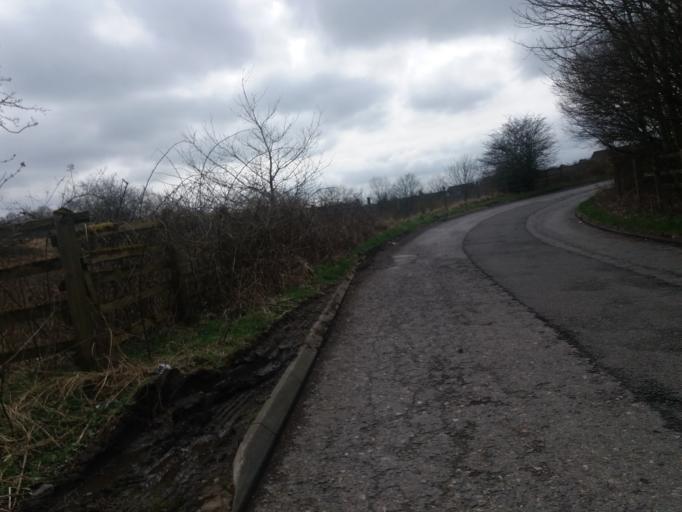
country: GB
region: England
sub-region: Lancashire
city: Chorley
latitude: 53.6559
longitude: -2.6089
